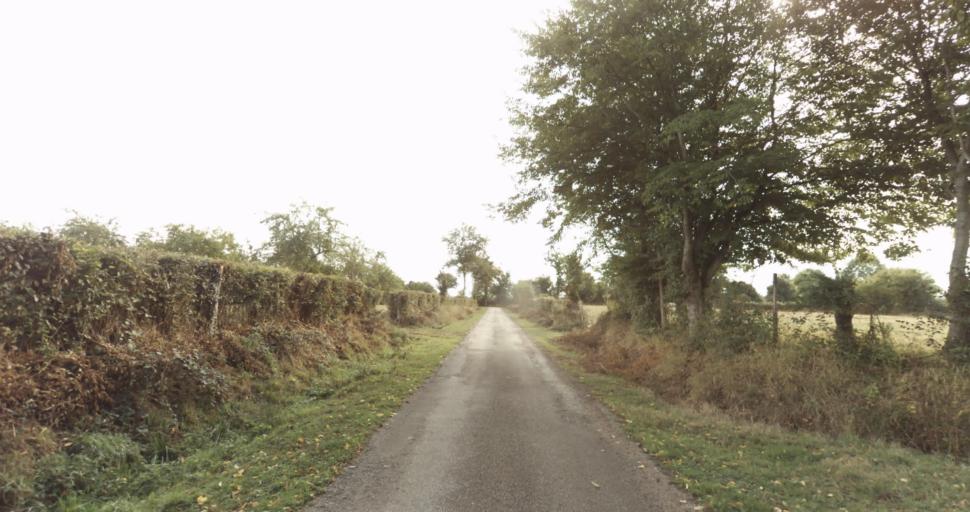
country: FR
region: Lower Normandy
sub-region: Departement de l'Orne
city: Vimoutiers
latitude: 48.8688
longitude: 0.1633
